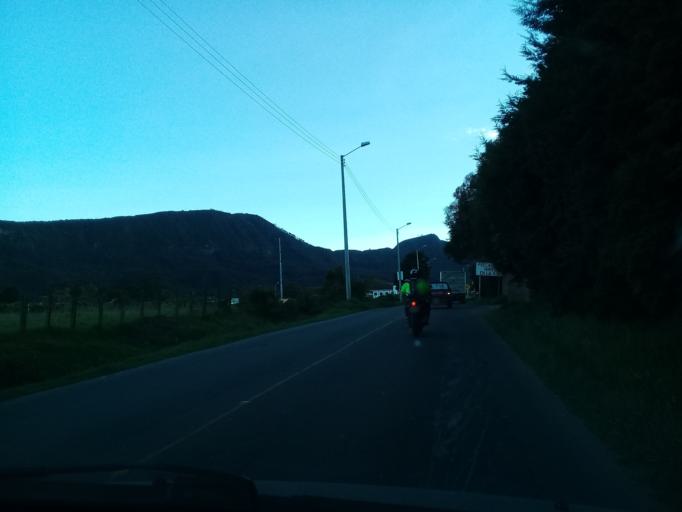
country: CO
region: Cundinamarca
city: Tenjo
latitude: 4.8456
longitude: -74.1318
